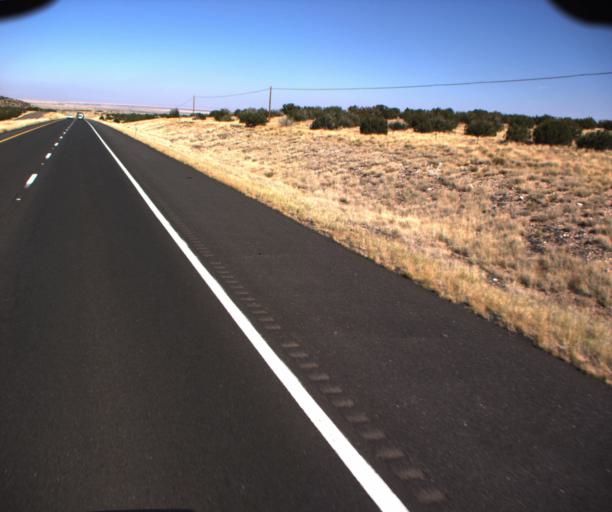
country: US
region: Arizona
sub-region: Coconino County
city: Flagstaff
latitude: 35.5024
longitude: -111.5501
